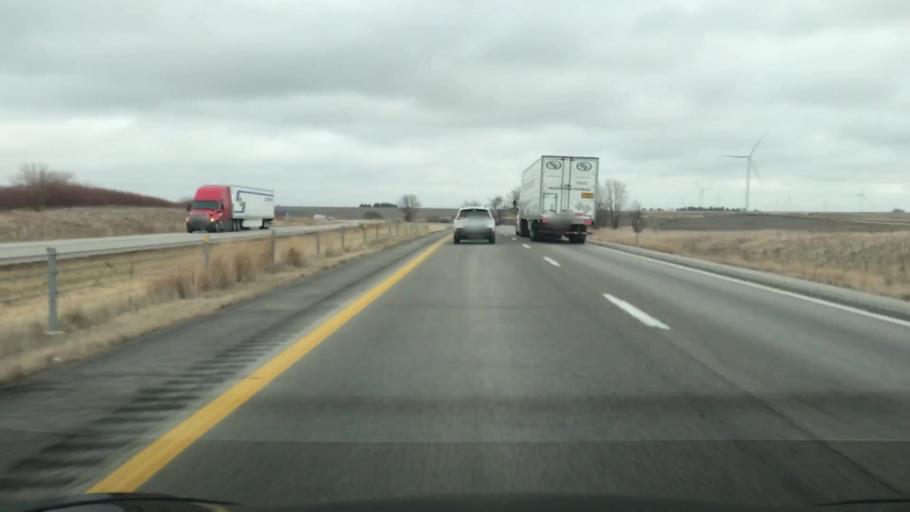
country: US
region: Iowa
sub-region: Guthrie County
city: Stuart
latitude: 41.4941
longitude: -94.3634
